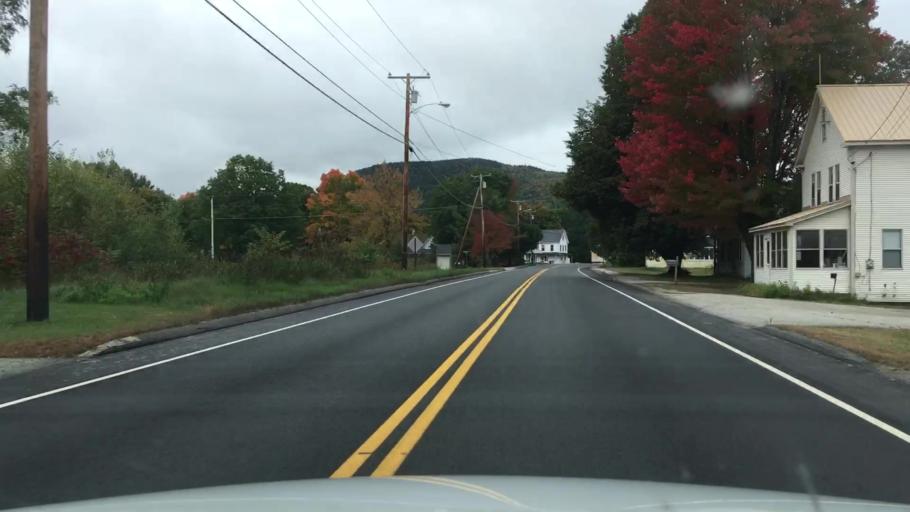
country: US
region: Maine
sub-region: Oxford County
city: Bethel
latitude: 44.4036
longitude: -70.8591
